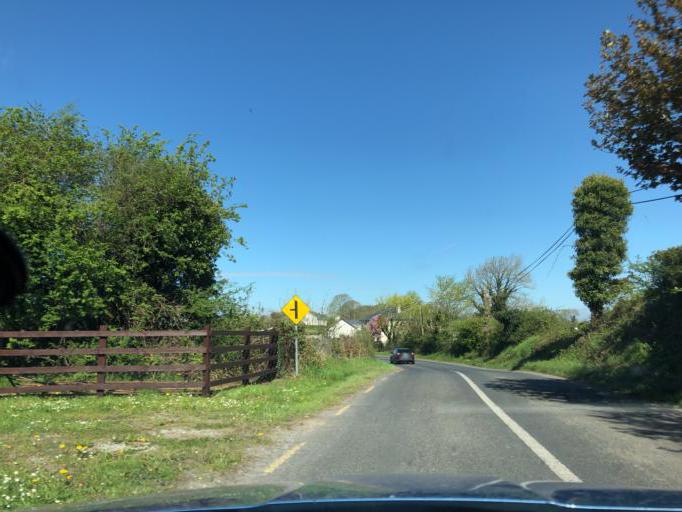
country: IE
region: Connaught
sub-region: County Galway
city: Portumna
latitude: 53.1343
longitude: -8.3585
